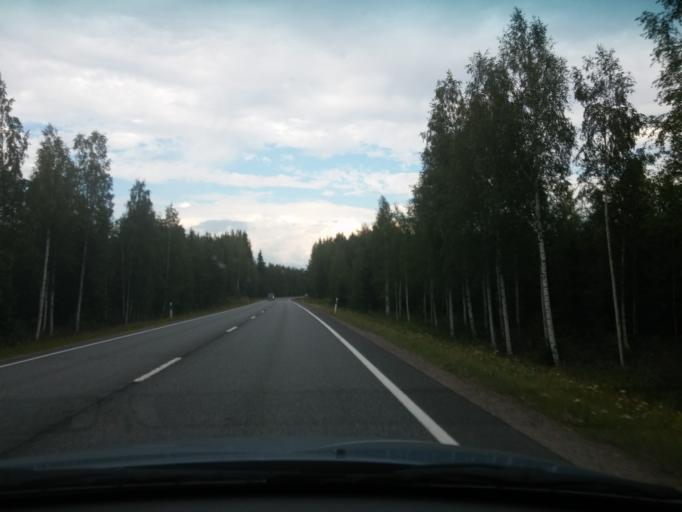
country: FI
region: Haeme
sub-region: Riihimaeki
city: Riihimaeki
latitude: 60.7442
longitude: 24.6979
